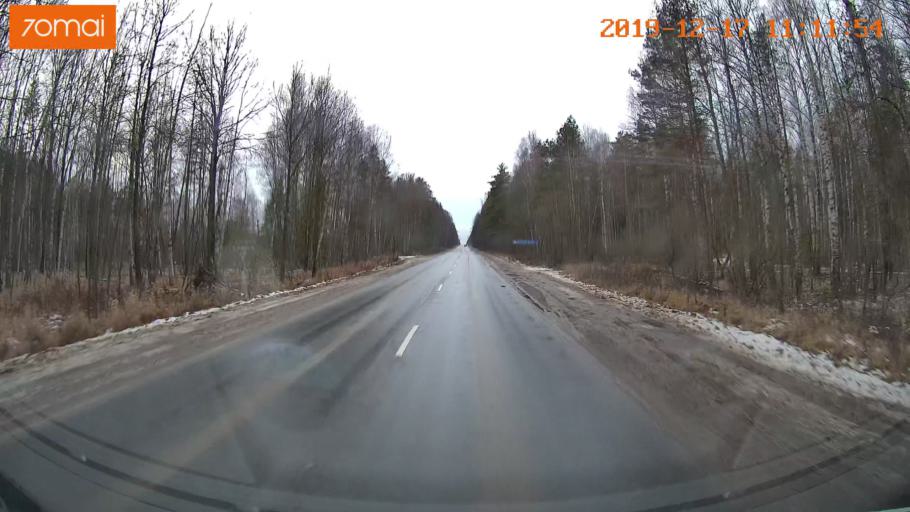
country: RU
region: Vladimir
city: Gus'-Khrustal'nyy
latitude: 55.5824
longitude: 40.6335
